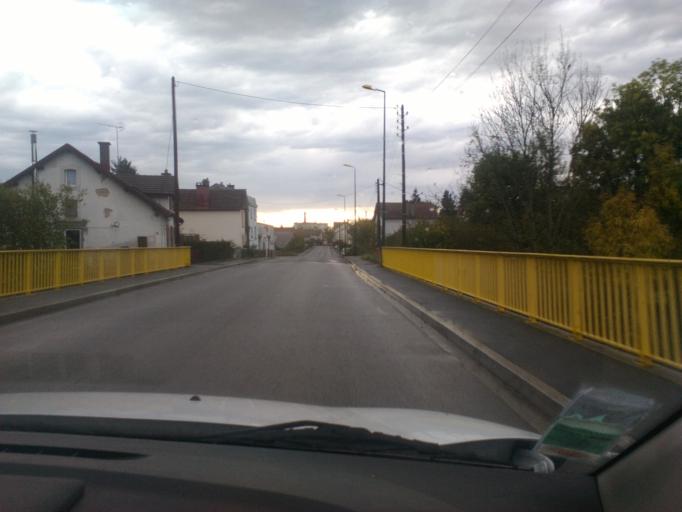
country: FR
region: Lorraine
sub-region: Departement des Vosges
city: Nomexy
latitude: 48.3104
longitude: 6.3769
